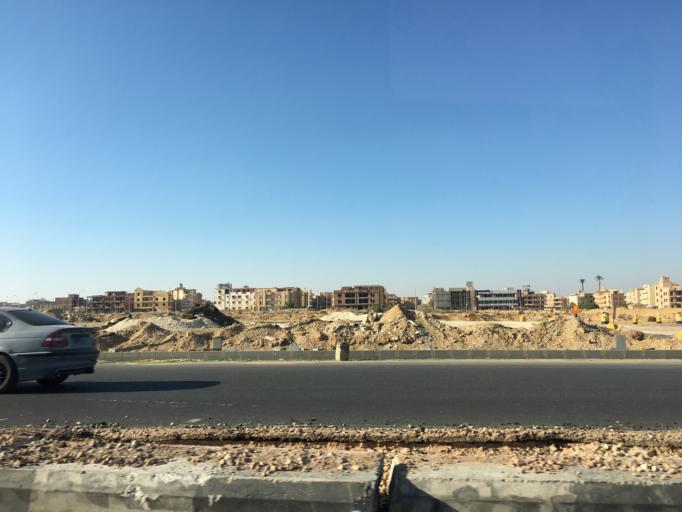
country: EG
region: Al Jizah
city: Madinat Sittah Uktubar
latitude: 29.9910
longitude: 30.9453
